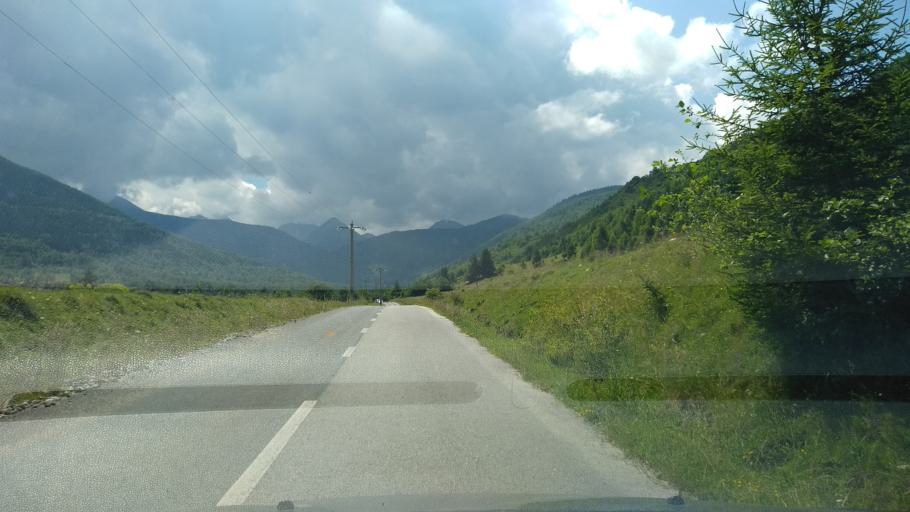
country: RO
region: Hunedoara
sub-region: Comuna Rau de Mori
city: Rau de Mori
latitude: 45.4585
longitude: 22.8980
